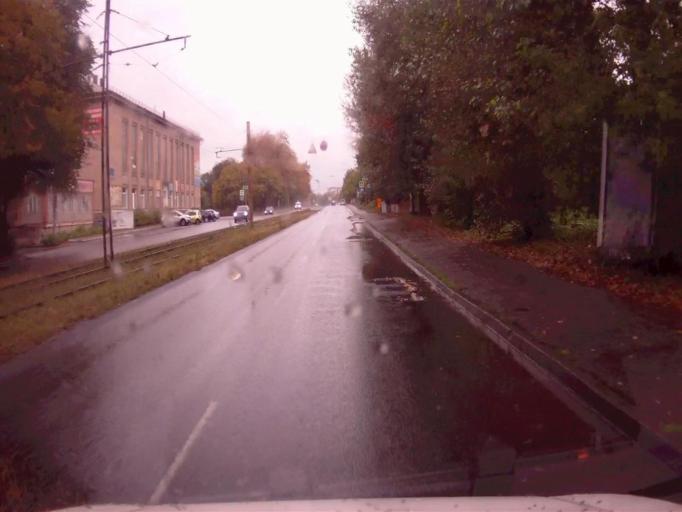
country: RU
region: Chelyabinsk
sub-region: Gorod Chelyabinsk
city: Chelyabinsk
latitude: 55.1798
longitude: 61.4147
